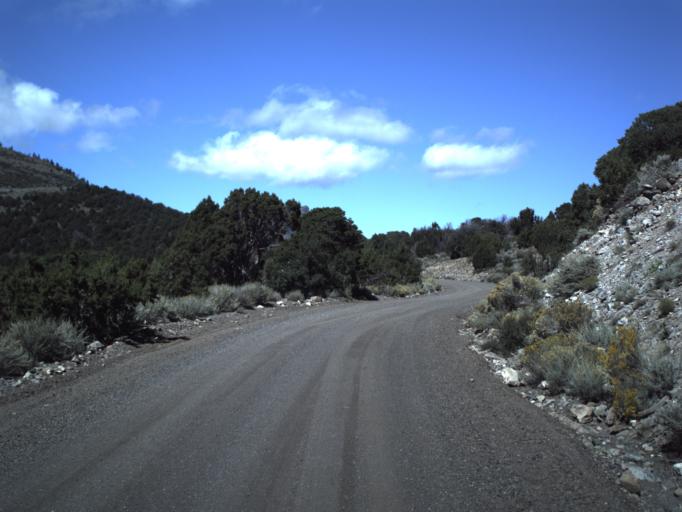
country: US
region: Utah
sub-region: Piute County
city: Junction
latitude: 38.2482
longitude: -112.3127
